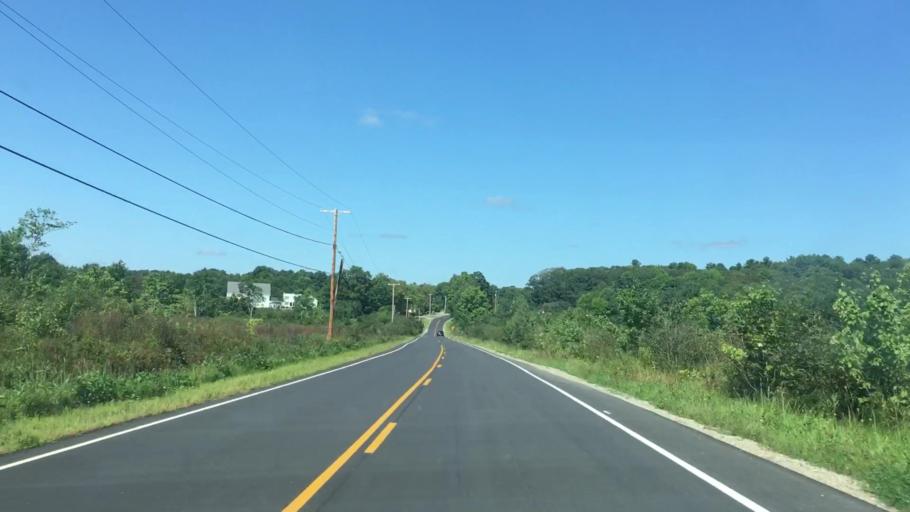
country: US
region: Maine
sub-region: Sagadahoc County
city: Topsham
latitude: 43.9776
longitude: -69.9812
